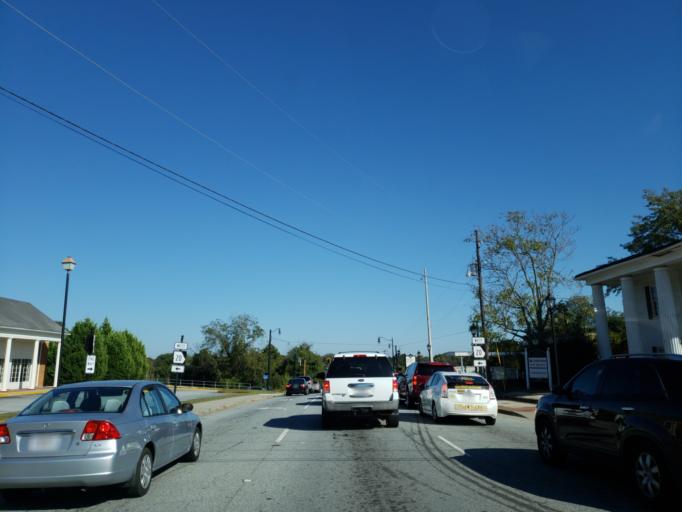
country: US
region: Georgia
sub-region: Gwinnett County
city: Lawrenceville
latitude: 33.9564
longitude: -83.9868
